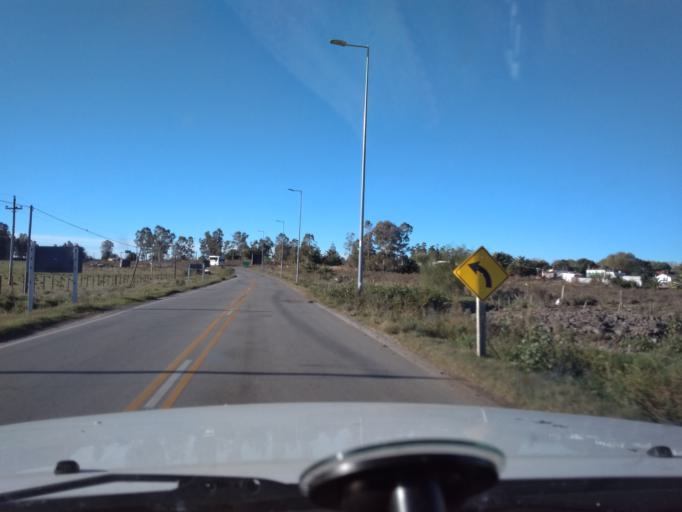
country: UY
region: Canelones
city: San Bautista
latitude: -34.4367
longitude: -55.9623
